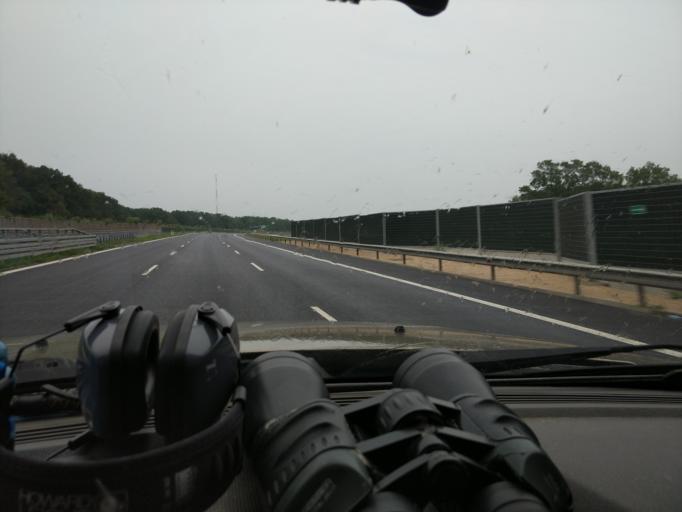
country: PL
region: Masovian Voivodeship
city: Zielonka
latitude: 52.3426
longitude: 21.1564
